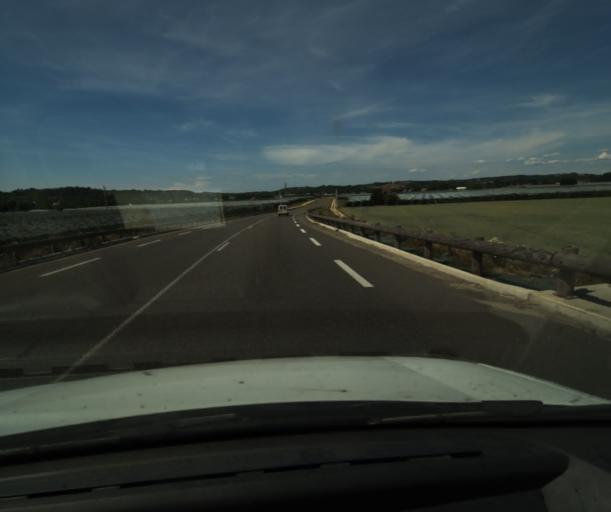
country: FR
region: Midi-Pyrenees
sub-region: Departement du Tarn-et-Garonne
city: Moissac
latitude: 44.0931
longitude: 1.1127
